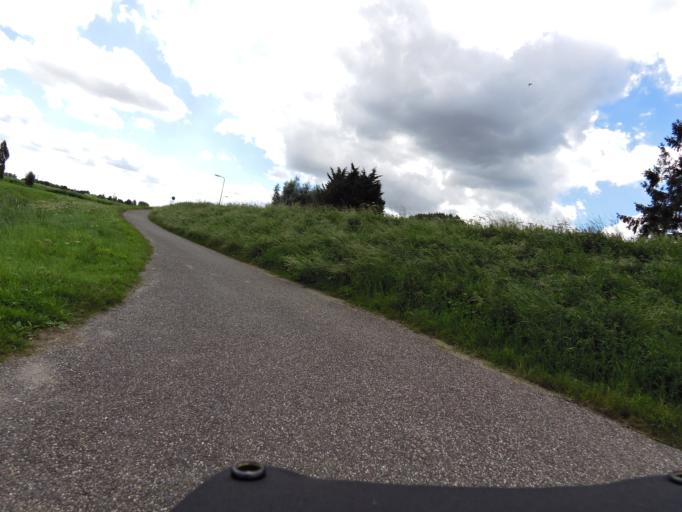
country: NL
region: South Holland
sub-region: Gemeente Spijkenisse
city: Spijkenisse
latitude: 51.8308
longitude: 4.3528
